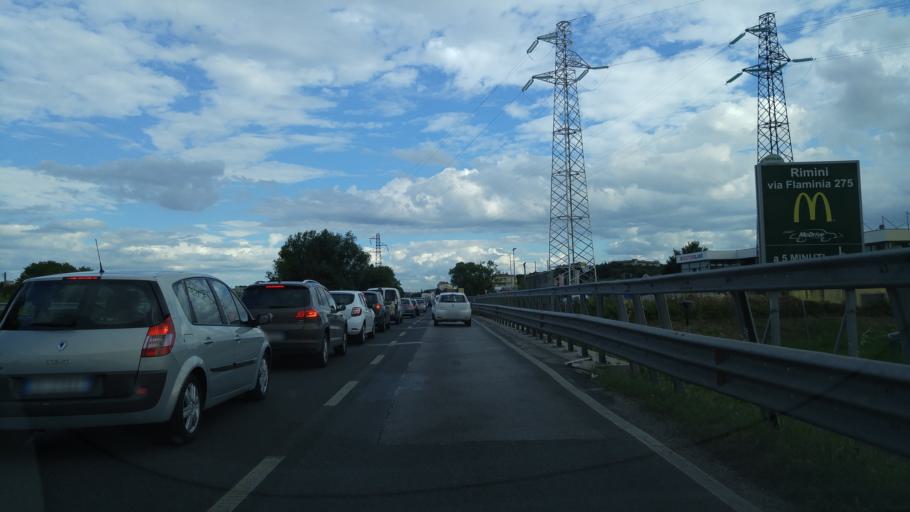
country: IT
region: Emilia-Romagna
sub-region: Provincia di Rimini
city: Rimini
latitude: 44.0510
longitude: 12.5475
